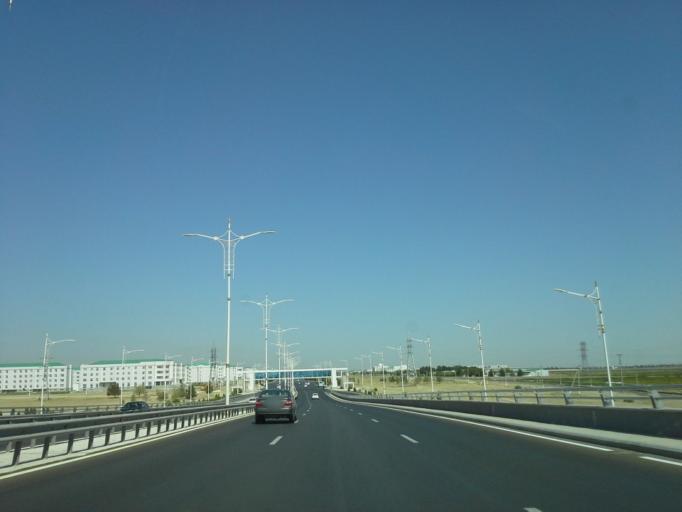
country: TM
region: Ahal
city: Ashgabat
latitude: 37.9785
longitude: 58.3414
